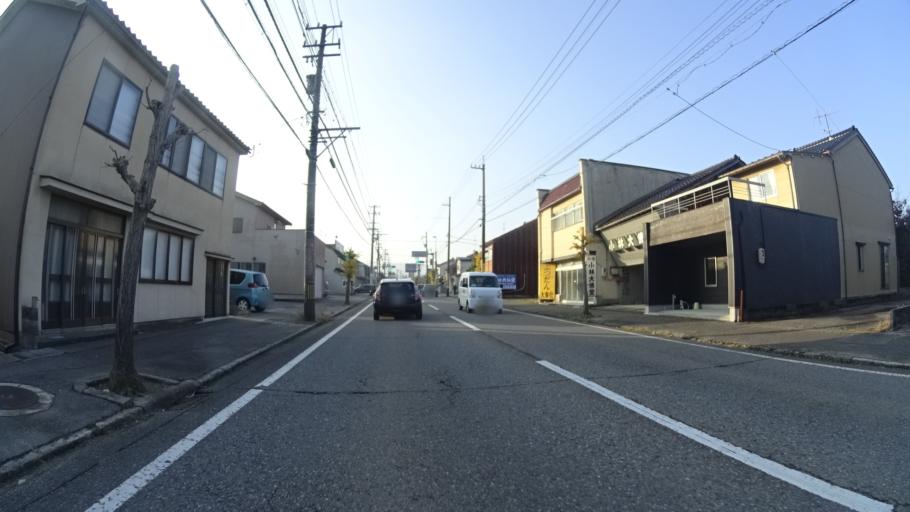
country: JP
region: Ishikawa
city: Nanao
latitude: 37.0403
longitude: 136.9694
